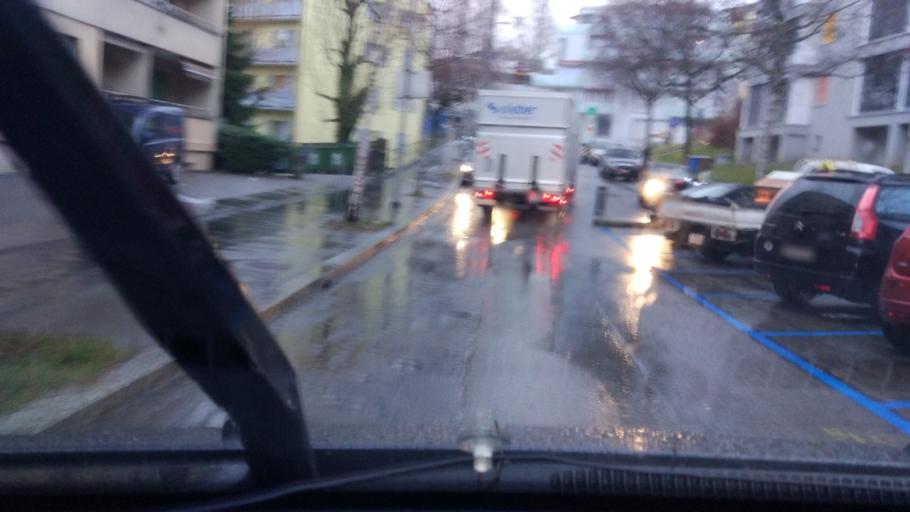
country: CH
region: Vaud
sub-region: Lausanne District
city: Blecherette
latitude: 46.5401
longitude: 6.6315
